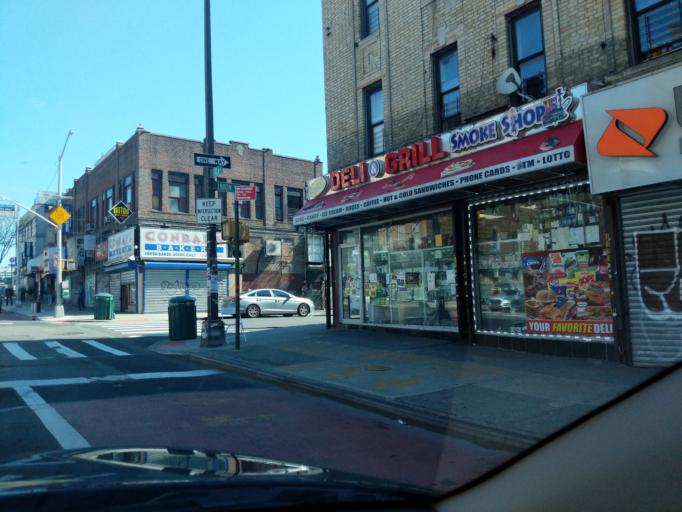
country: US
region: New York
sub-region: Kings County
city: Brooklyn
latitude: 40.6677
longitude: -73.9312
